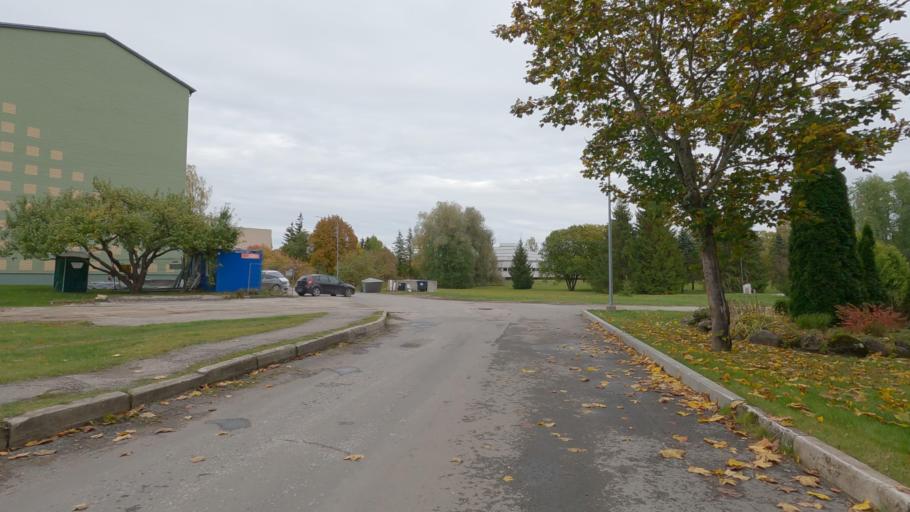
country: EE
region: Raplamaa
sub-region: Rapla vald
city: Rapla
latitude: 58.9978
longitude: 24.7952
